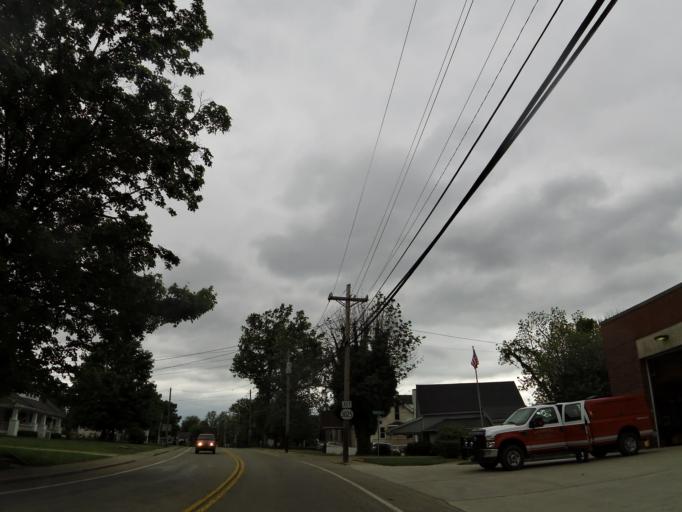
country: US
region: Kentucky
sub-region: Grant County
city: Williamstown
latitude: 38.6408
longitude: -84.5600
